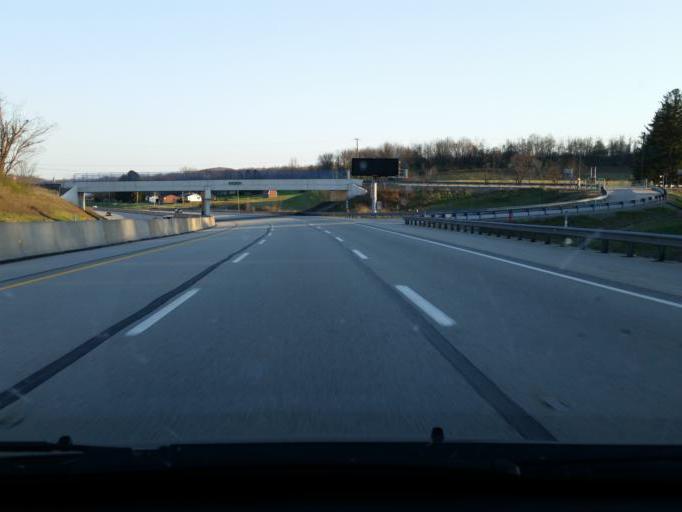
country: US
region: Pennsylvania
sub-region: Westmoreland County
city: New Stanton
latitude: 40.2533
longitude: -79.6425
